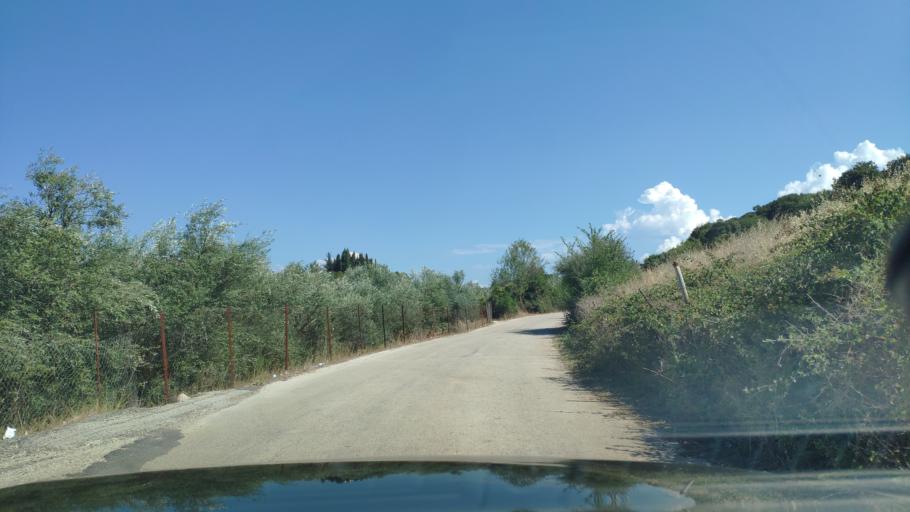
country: GR
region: West Greece
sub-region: Nomos Aitolias kai Akarnanias
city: Katouna
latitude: 38.7974
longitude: 21.1130
